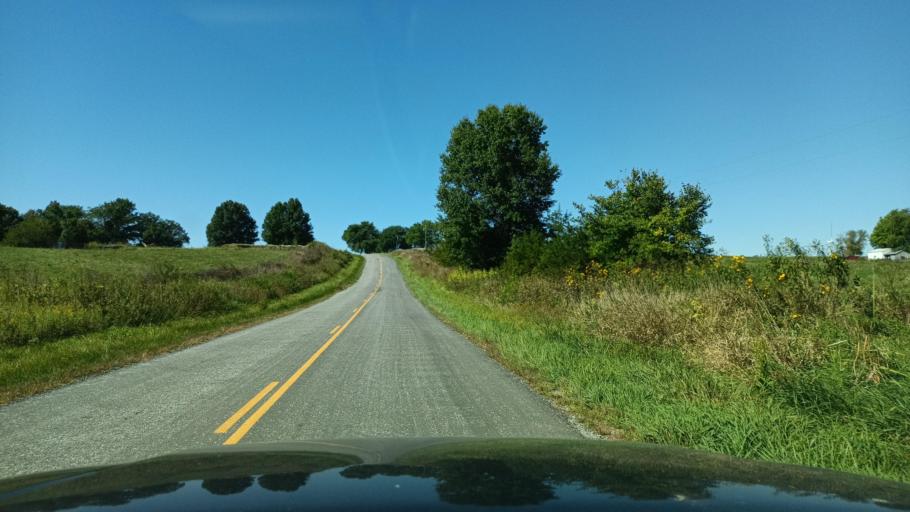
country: US
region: Missouri
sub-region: Adair County
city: Kirksville
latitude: 40.3308
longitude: -92.5122
